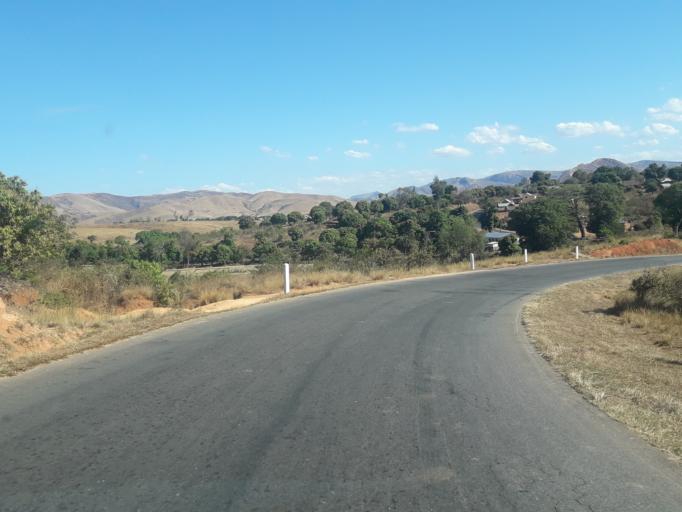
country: MG
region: Betsiboka
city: Maevatanana
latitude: -17.5924
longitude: 46.9350
